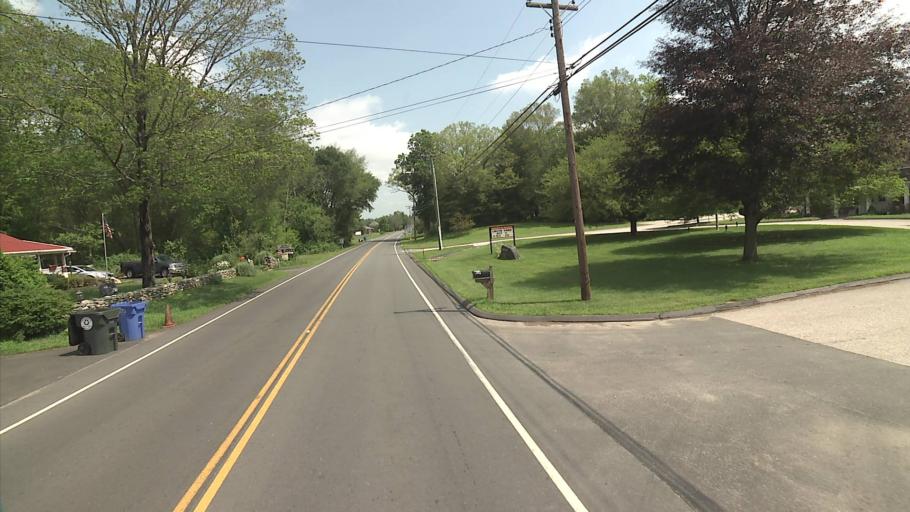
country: US
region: Connecticut
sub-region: New London County
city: Preston City
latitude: 41.5678
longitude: -71.8677
